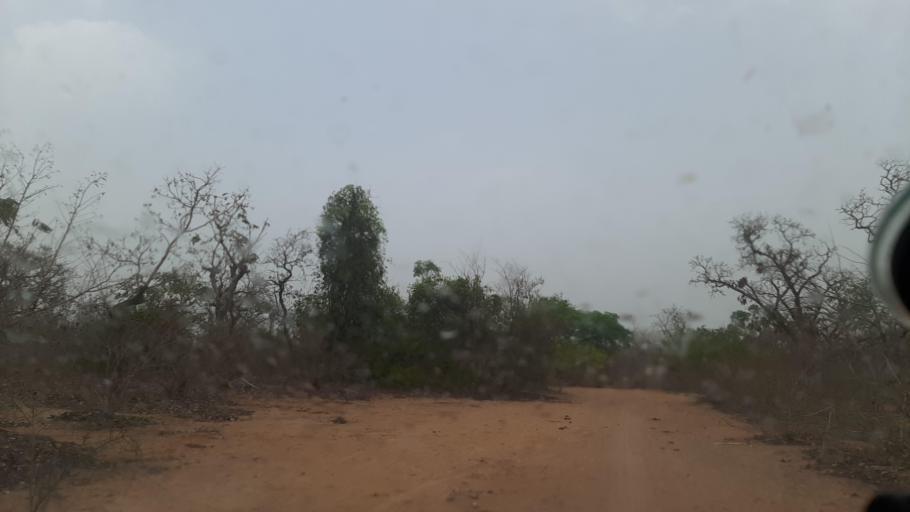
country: BF
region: Boucle du Mouhoun
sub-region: Province des Banwa
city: Salanso
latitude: 11.8628
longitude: -4.4381
